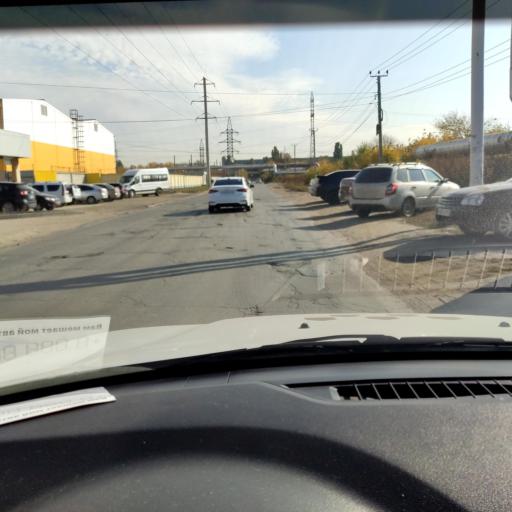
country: RU
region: Samara
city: Tol'yatti
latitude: 53.5455
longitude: 49.4395
